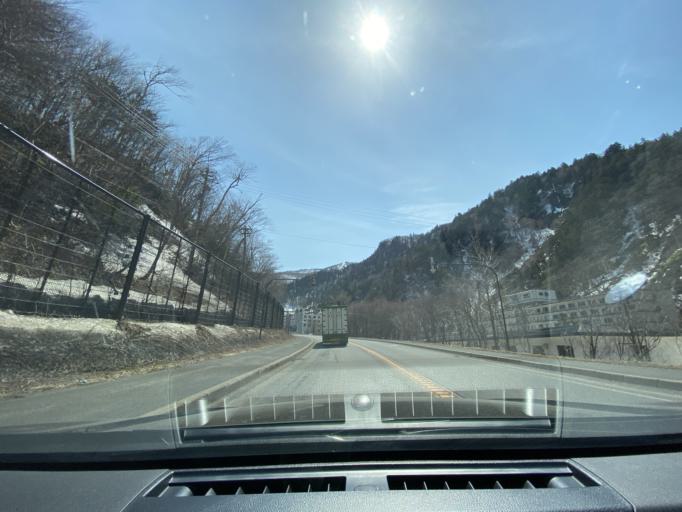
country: JP
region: Hokkaido
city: Kamikawa
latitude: 43.7321
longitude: 142.9420
